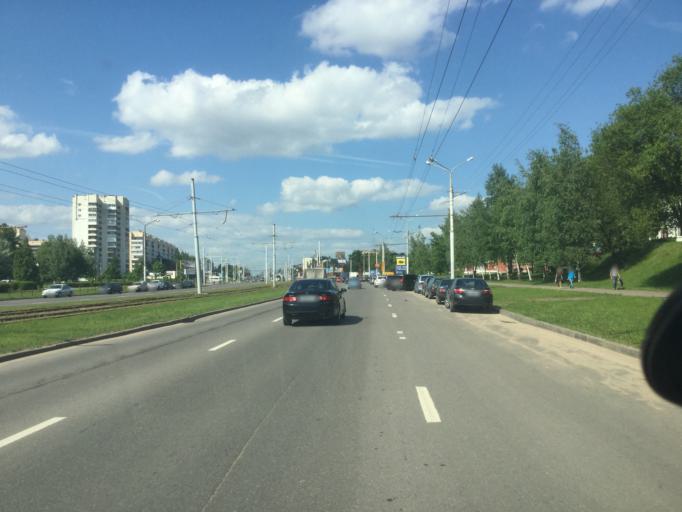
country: BY
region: Vitebsk
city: Vitebsk
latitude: 55.1656
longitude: 30.2403
